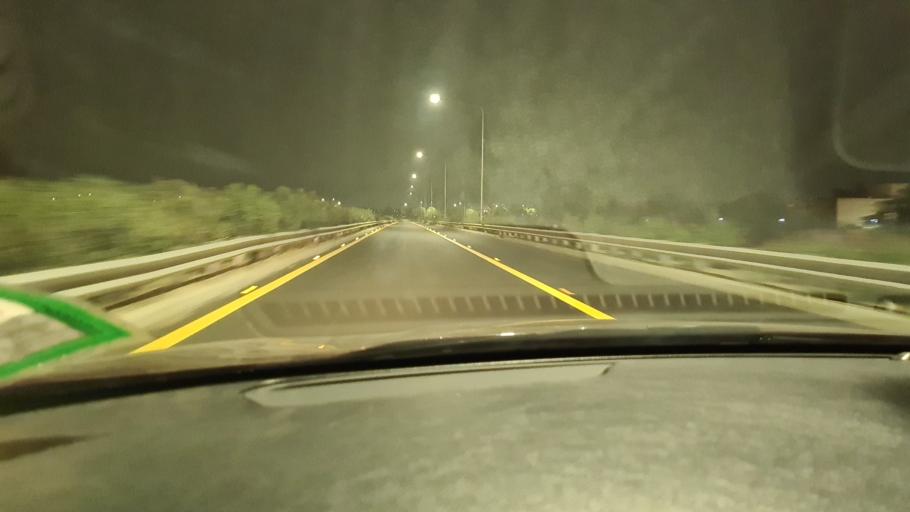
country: SA
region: Eastern Province
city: Al Jubayl
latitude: 27.1199
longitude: 49.5416
